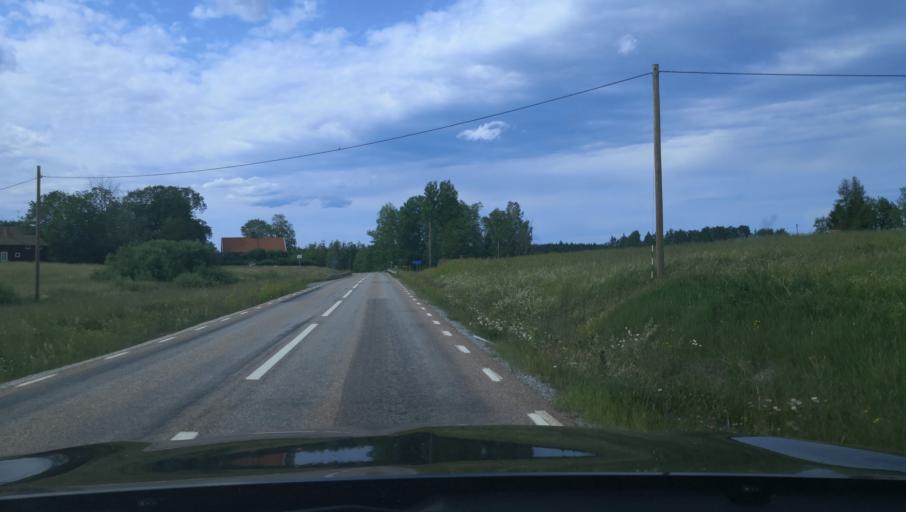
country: SE
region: Dalarna
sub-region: Avesta Kommun
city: Avesta
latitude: 59.9848
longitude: 16.1217
